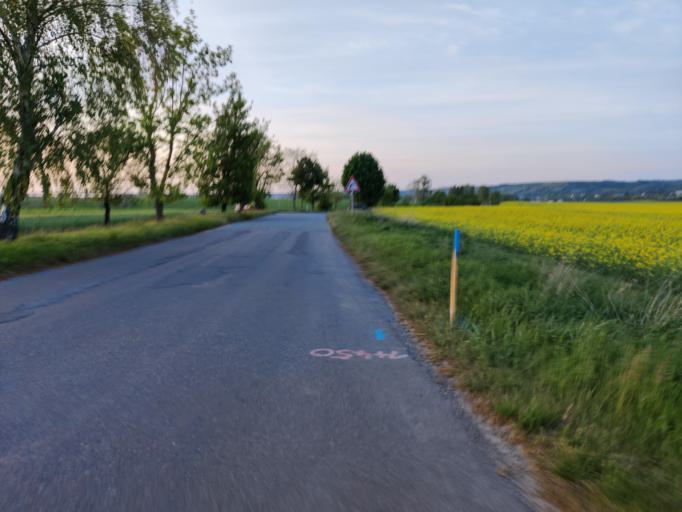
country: DE
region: Saxony-Anhalt
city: Karsdorf
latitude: 51.2576
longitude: 11.6439
